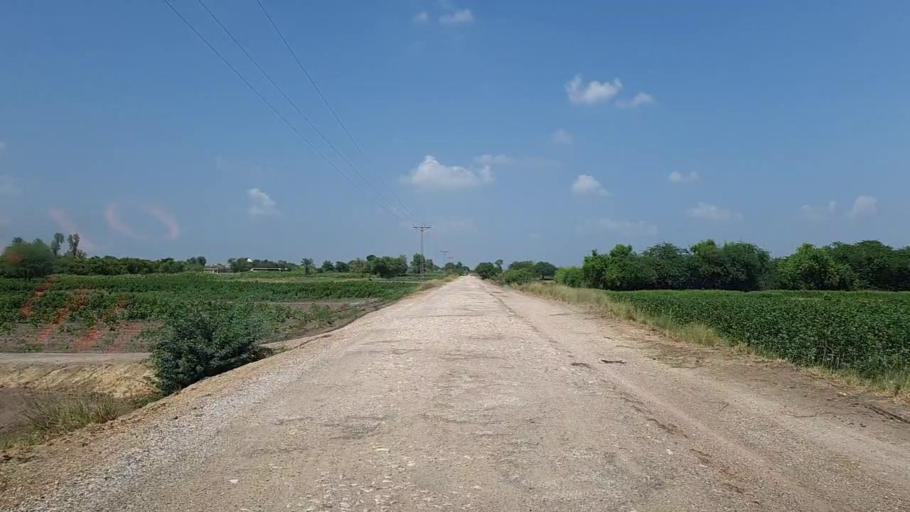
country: PK
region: Sindh
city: Kandiaro
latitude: 26.9956
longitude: 68.2520
